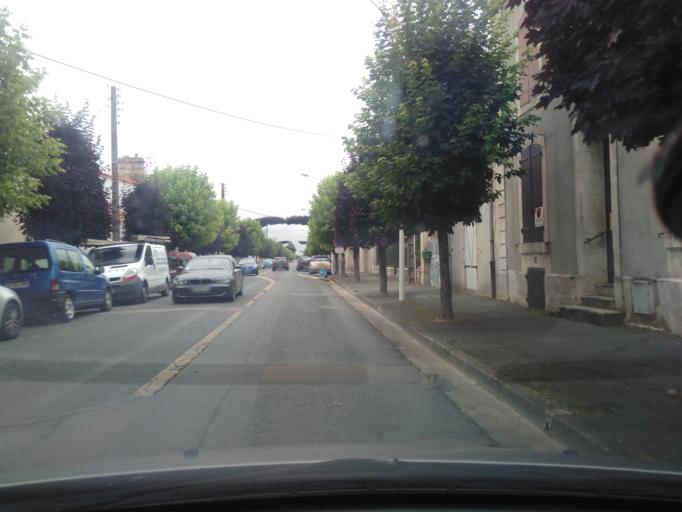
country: FR
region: Pays de la Loire
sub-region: Departement de la Vendee
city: Lucon
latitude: 46.4593
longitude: -1.1687
